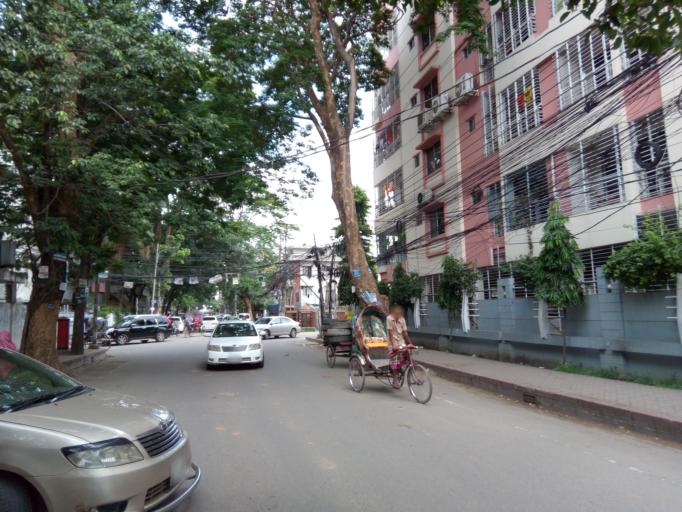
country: BD
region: Dhaka
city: Azimpur
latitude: 23.7457
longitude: 90.3746
